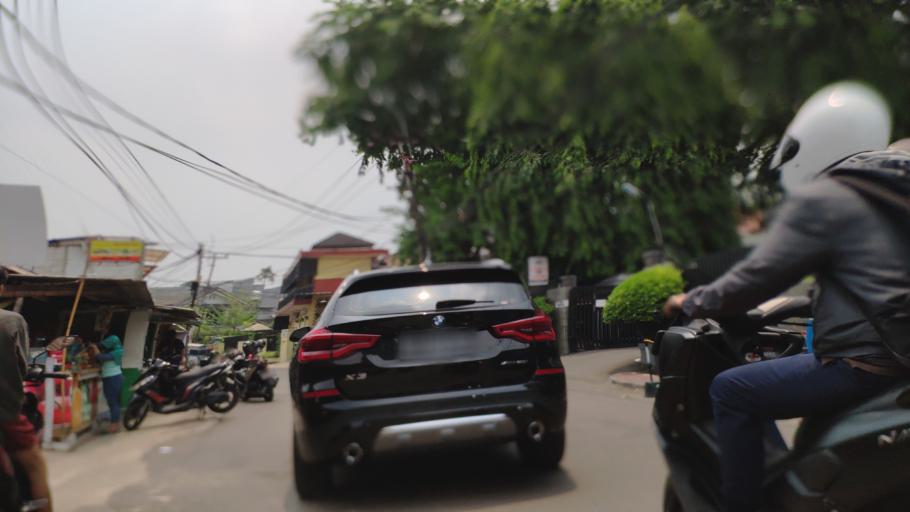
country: ID
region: Banten
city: South Tangerang
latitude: -6.2603
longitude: 106.7691
